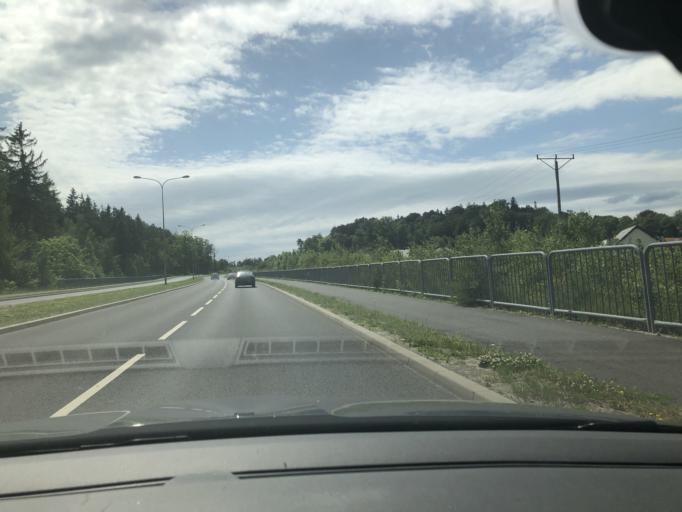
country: PL
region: Lower Silesian Voivodeship
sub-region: Jelenia Gora
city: Jelenia Gora
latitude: 50.8951
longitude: 15.7674
